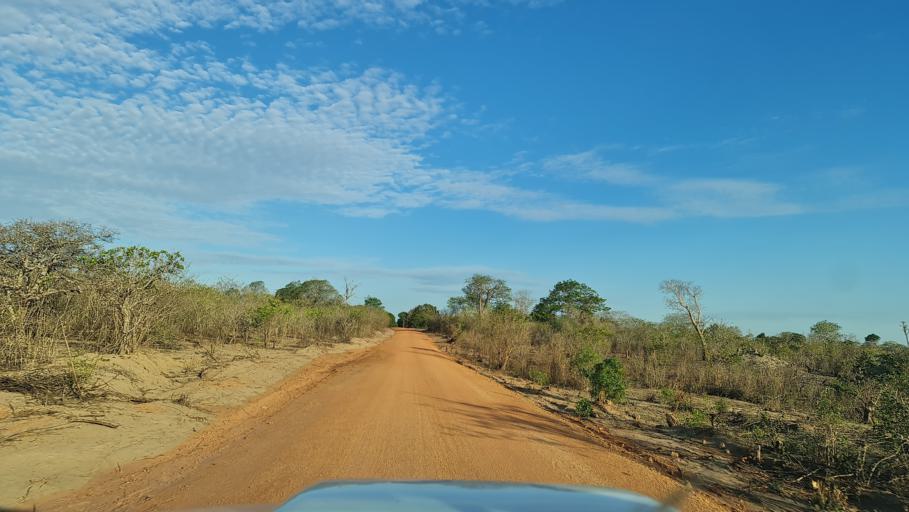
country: MZ
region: Nampula
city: Nacala
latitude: -14.6953
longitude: 40.3220
